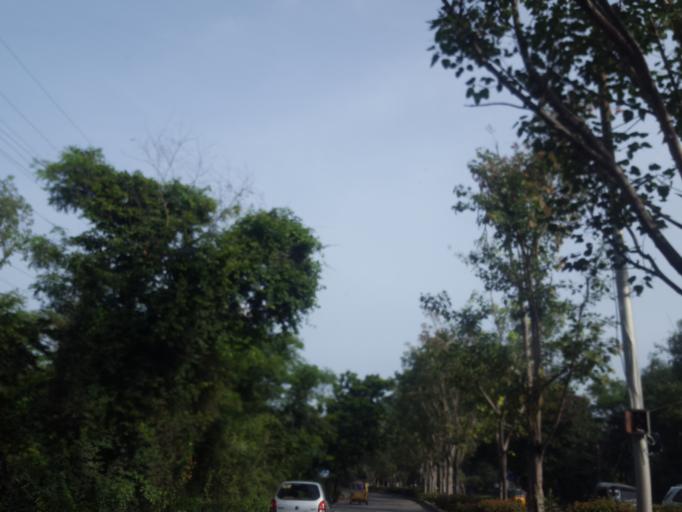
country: IN
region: Telangana
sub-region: Medak
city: Serilingampalle
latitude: 17.4643
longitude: 78.3343
